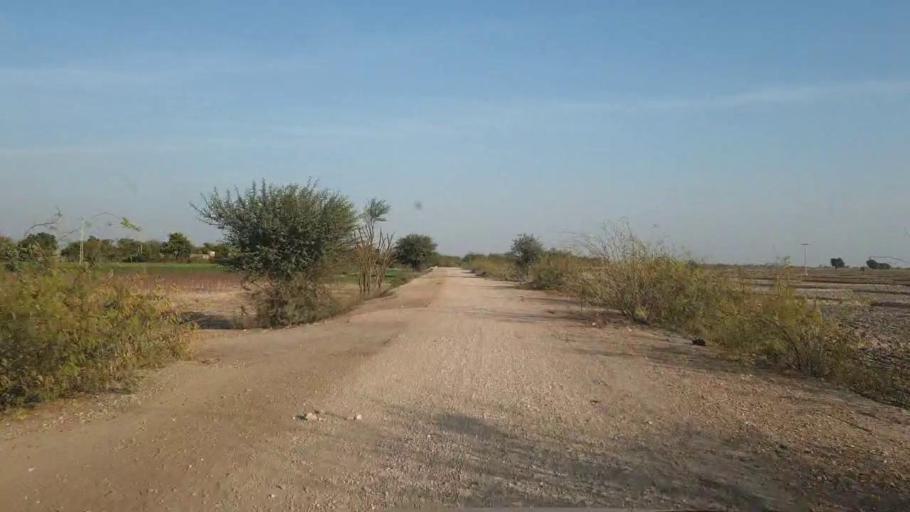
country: PK
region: Sindh
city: Chambar
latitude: 25.2387
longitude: 68.8020
